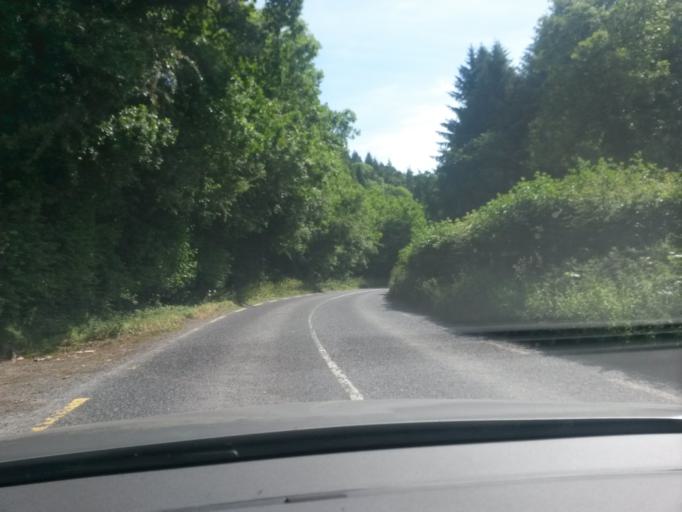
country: IE
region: Leinster
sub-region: Kildare
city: Eadestown
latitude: 53.1848
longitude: -6.5575
